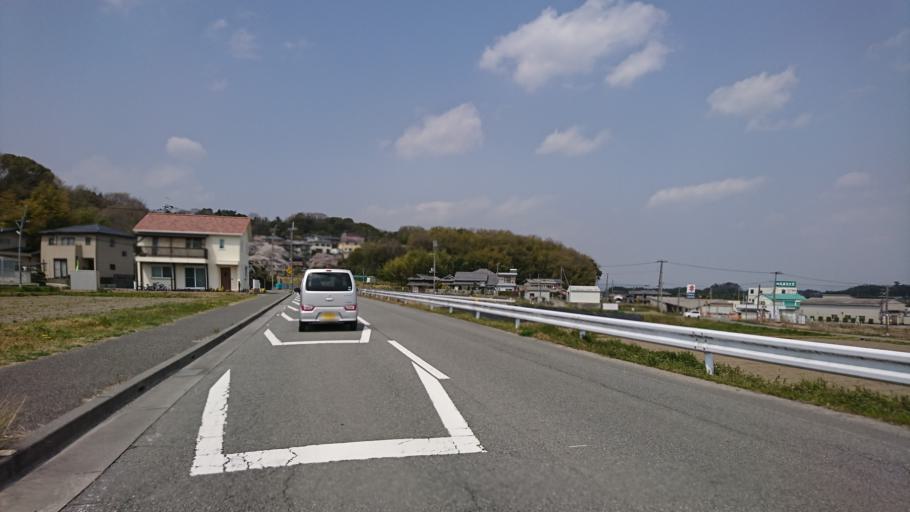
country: JP
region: Hyogo
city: Ono
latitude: 34.8405
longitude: 134.9102
